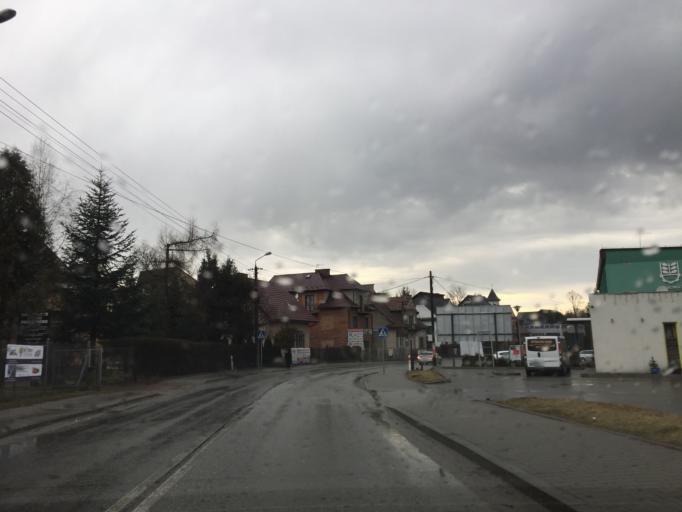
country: PL
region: Lesser Poland Voivodeship
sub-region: Powiat myslenicki
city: Sulkowice
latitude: 49.8430
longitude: 19.8019
